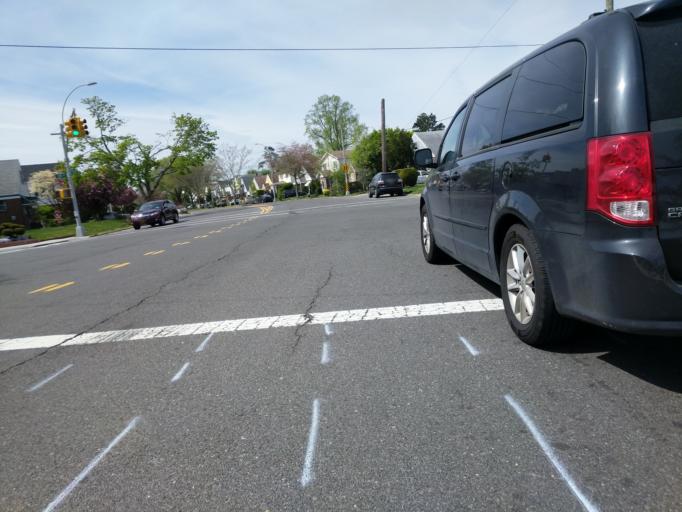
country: US
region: New York
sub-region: Nassau County
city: Elmont
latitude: 40.6814
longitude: -73.7363
